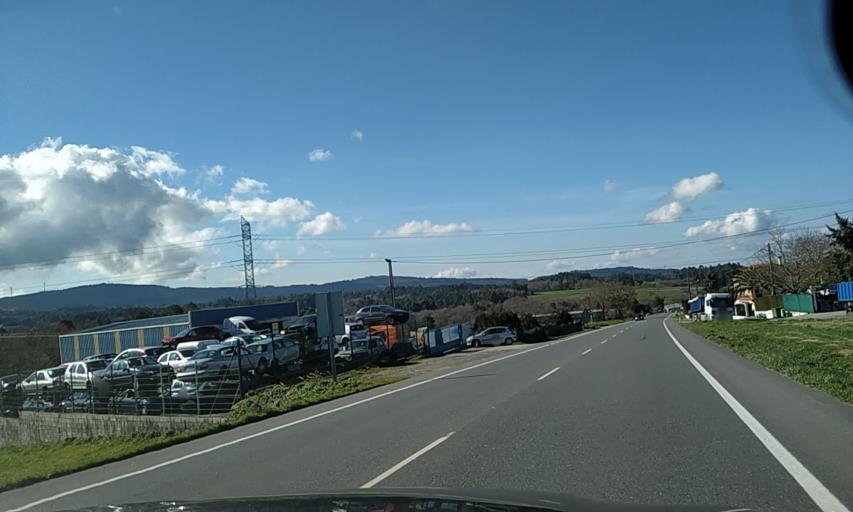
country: ES
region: Galicia
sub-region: Provincia de Pontevedra
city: Silleda
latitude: 42.7108
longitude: -8.2749
